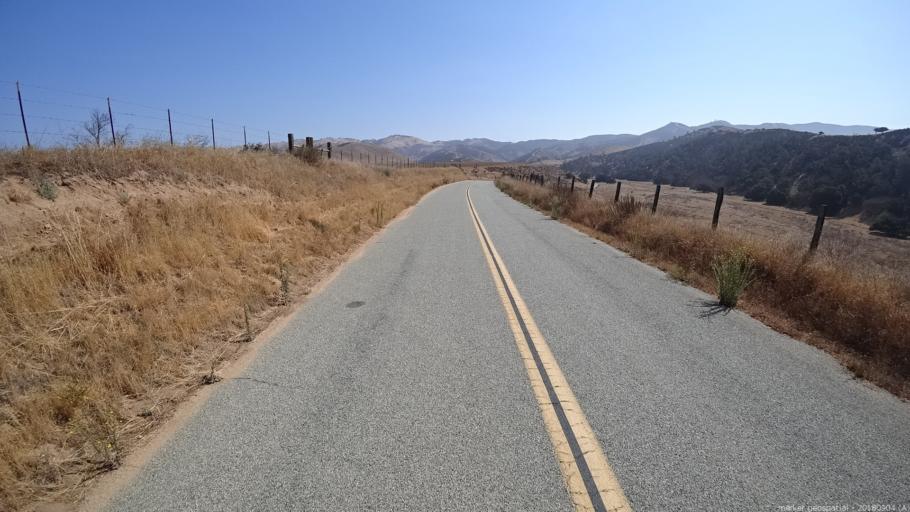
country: US
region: California
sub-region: Monterey County
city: Soledad
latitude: 36.5126
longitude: -121.3511
